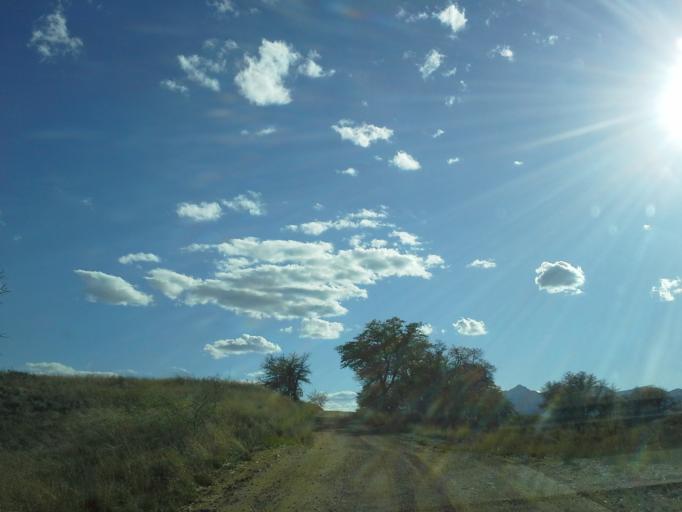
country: US
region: Arizona
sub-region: Pima County
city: Corona de Tucson
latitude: 31.7457
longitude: -110.7014
